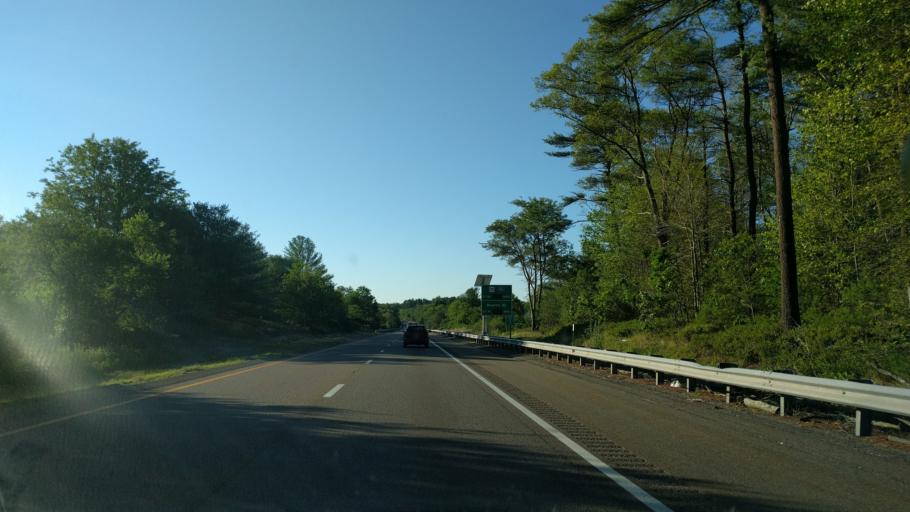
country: US
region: Massachusetts
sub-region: Bristol County
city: Raynham Center
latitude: 41.9268
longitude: -71.0008
